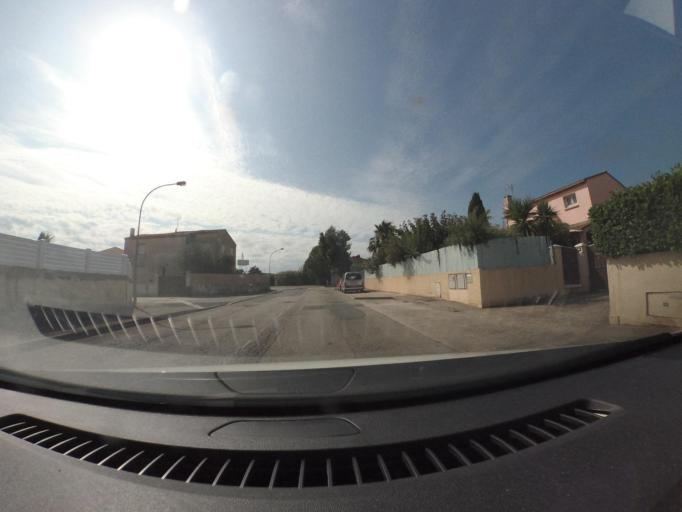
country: FR
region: Languedoc-Roussillon
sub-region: Departement de l'Herault
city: Baillargues
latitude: 43.6561
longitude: 4.0011
